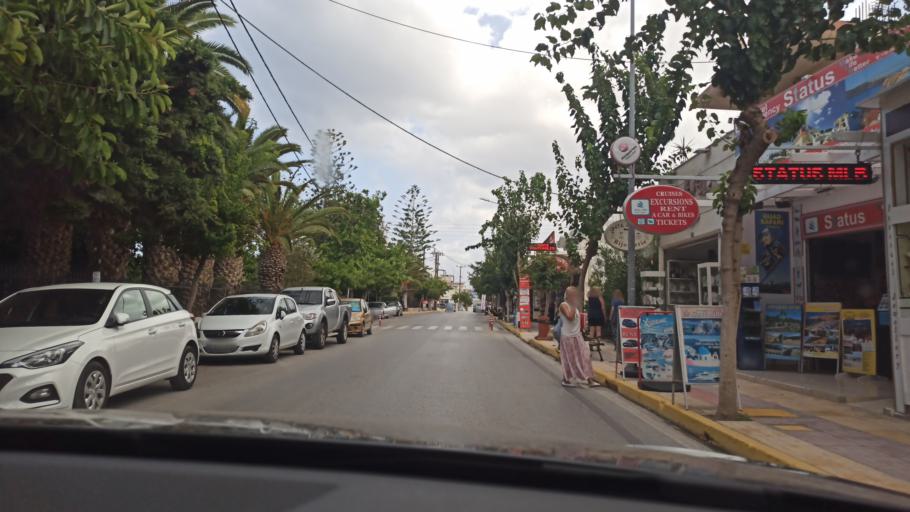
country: GR
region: Crete
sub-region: Nomos Irakleiou
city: Gazi
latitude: 35.3359
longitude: 25.0720
